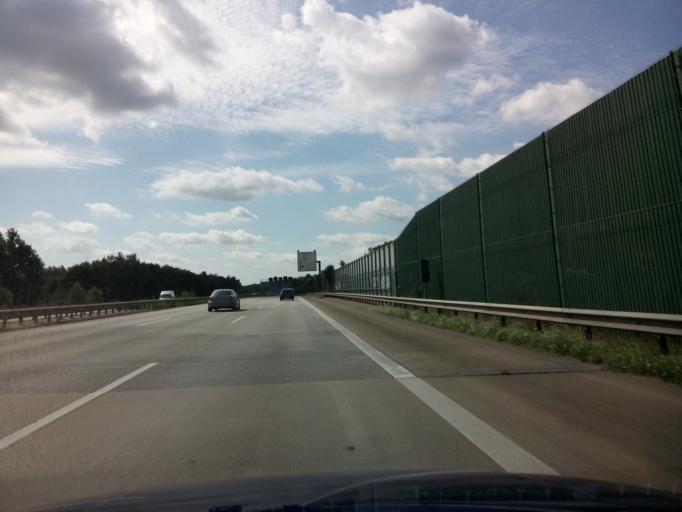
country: DE
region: Lower Saxony
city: Ritterhude
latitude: 53.1595
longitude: 8.7220
